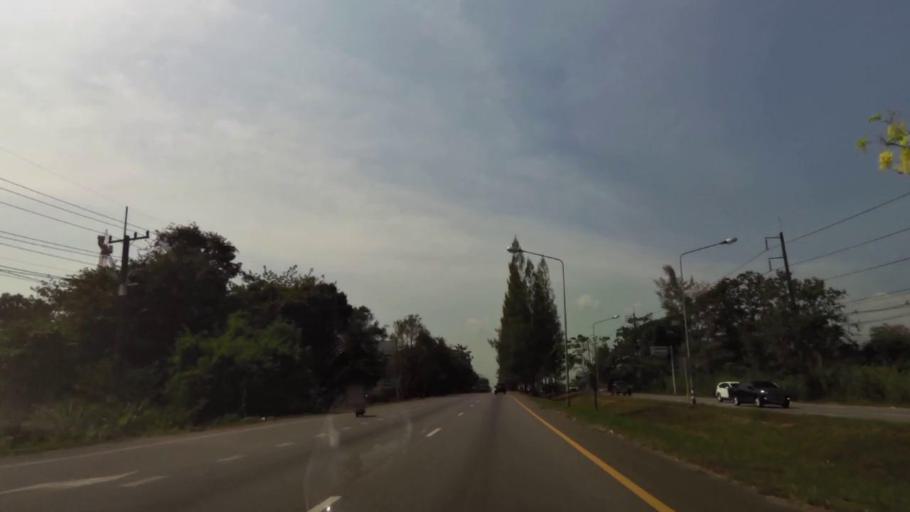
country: TH
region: Chanthaburi
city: Chanthaburi
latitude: 12.6646
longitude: 102.1098
